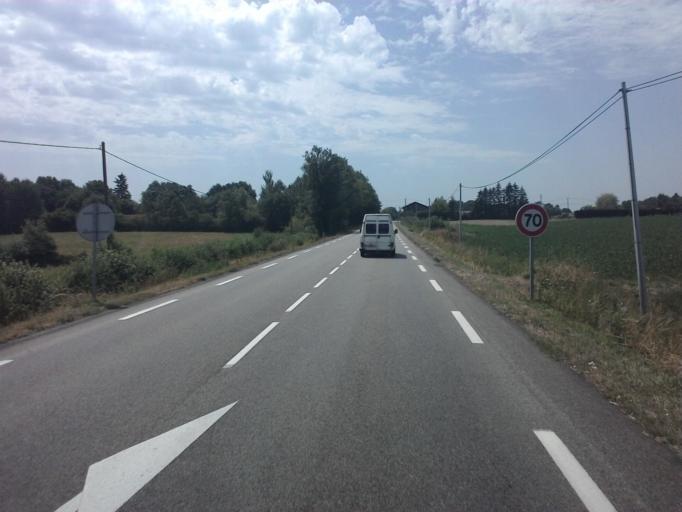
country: FR
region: Rhone-Alpes
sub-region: Departement de l'Ain
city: Saint-Etienne-du-Bois
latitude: 46.2972
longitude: 5.3004
